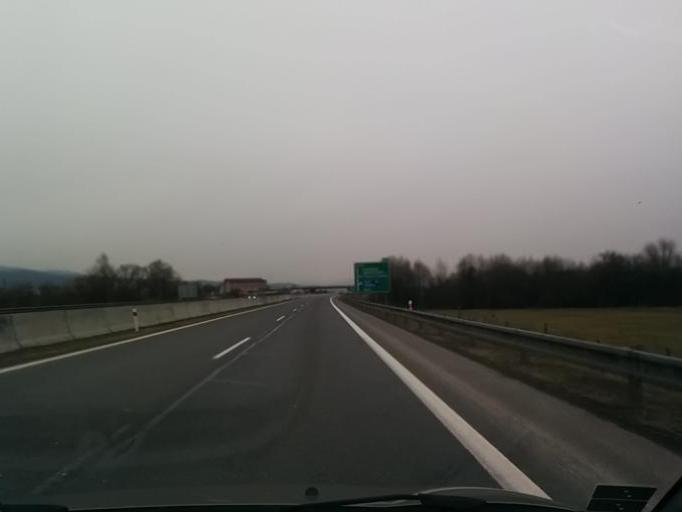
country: SK
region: Banskobystricky
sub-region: Okres Banska Bystrica
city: Zvolen
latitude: 48.6242
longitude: 19.1187
